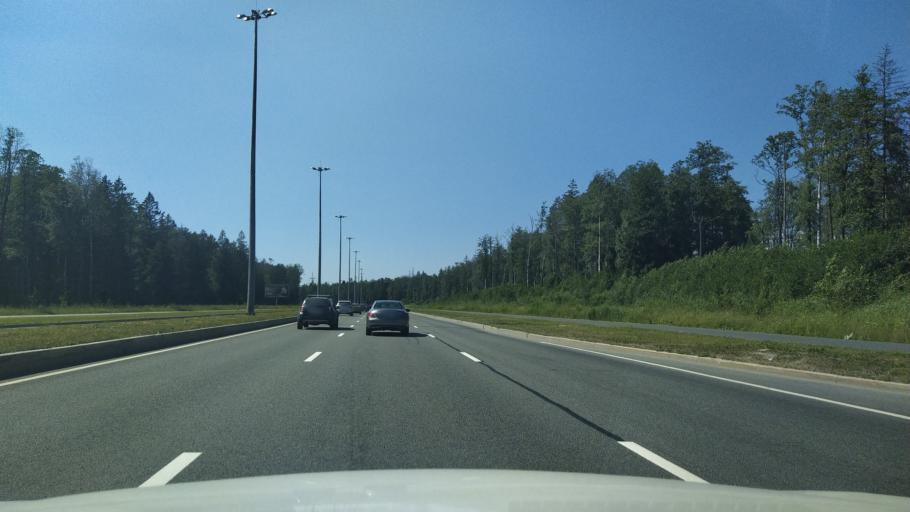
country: RU
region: St.-Petersburg
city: Levashovo
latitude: 60.0635
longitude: 30.2133
